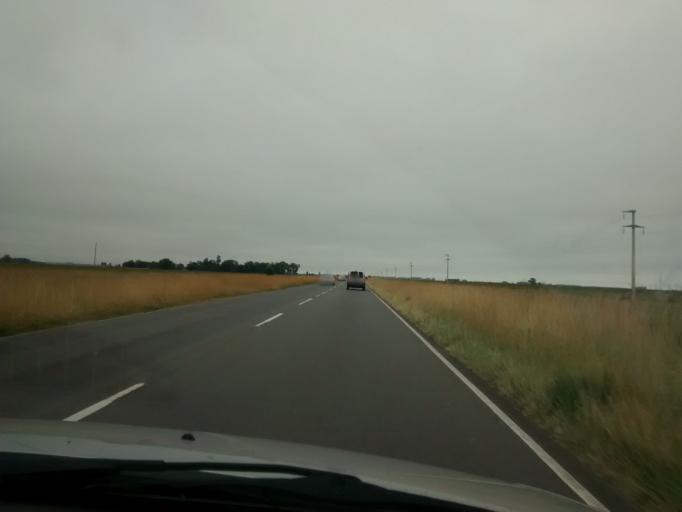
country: AR
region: Buenos Aires
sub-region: Partido de Ayacucho
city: Ayacucho
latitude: -37.0478
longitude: -58.5417
